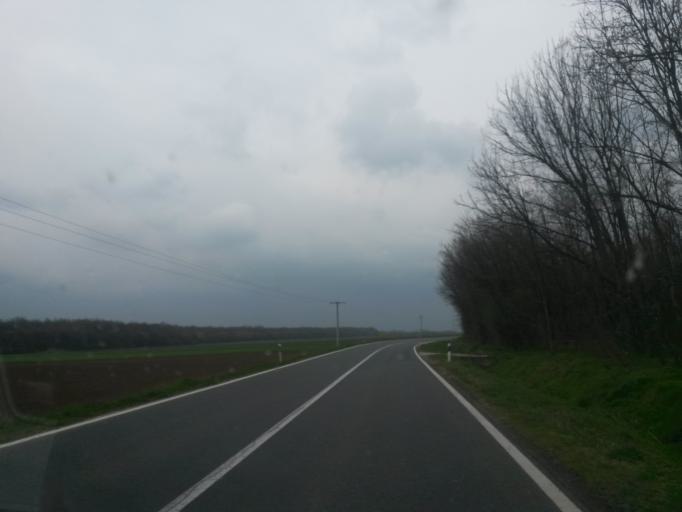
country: HR
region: Vukovarsko-Srijemska
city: Nijemci
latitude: 45.1988
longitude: 19.0178
